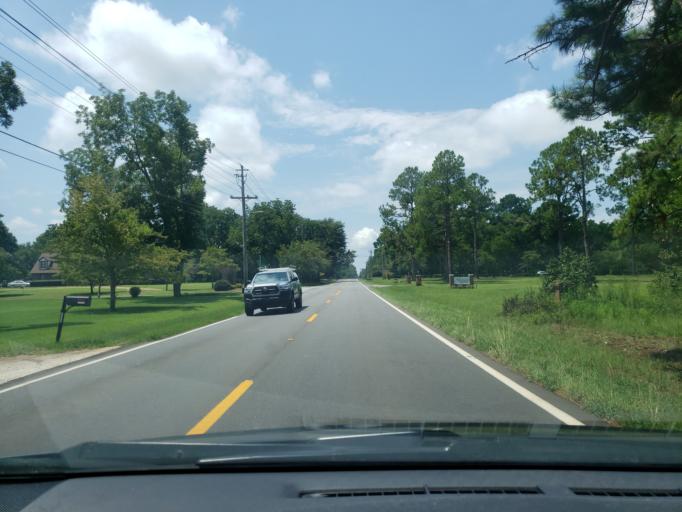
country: US
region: Georgia
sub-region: Dougherty County
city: Albany
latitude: 31.6131
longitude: -84.2680
